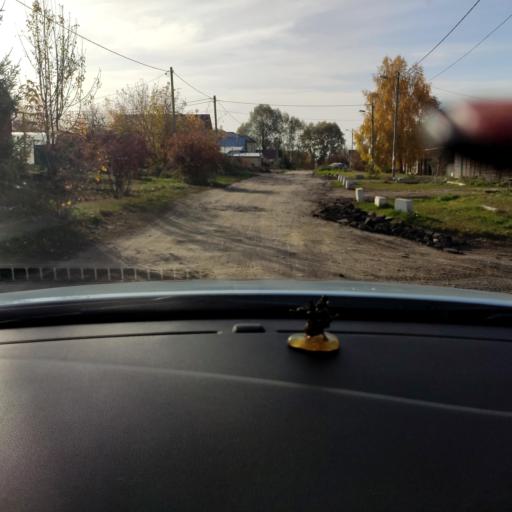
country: RU
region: Tatarstan
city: Vysokaya Gora
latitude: 55.7958
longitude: 49.2685
